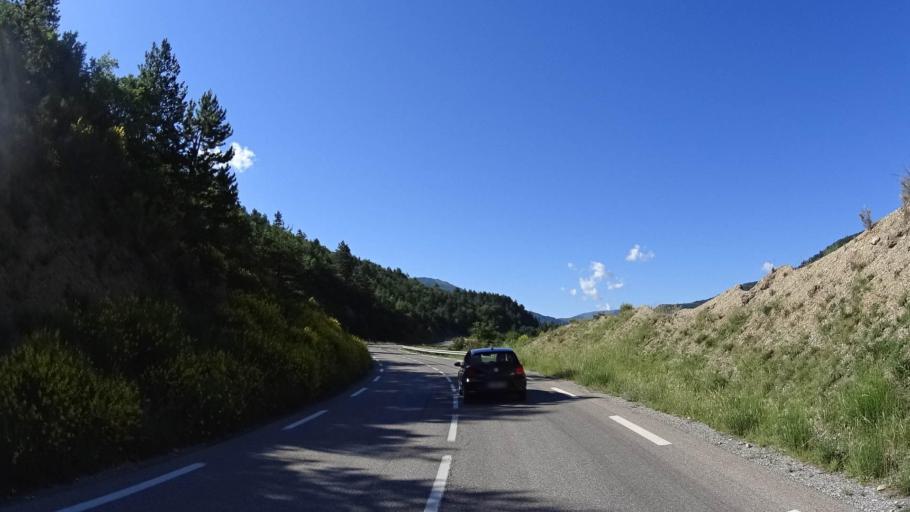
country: FR
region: Provence-Alpes-Cote d'Azur
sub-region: Departement des Alpes-de-Haute-Provence
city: Castellane
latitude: 43.9288
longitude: 6.5323
